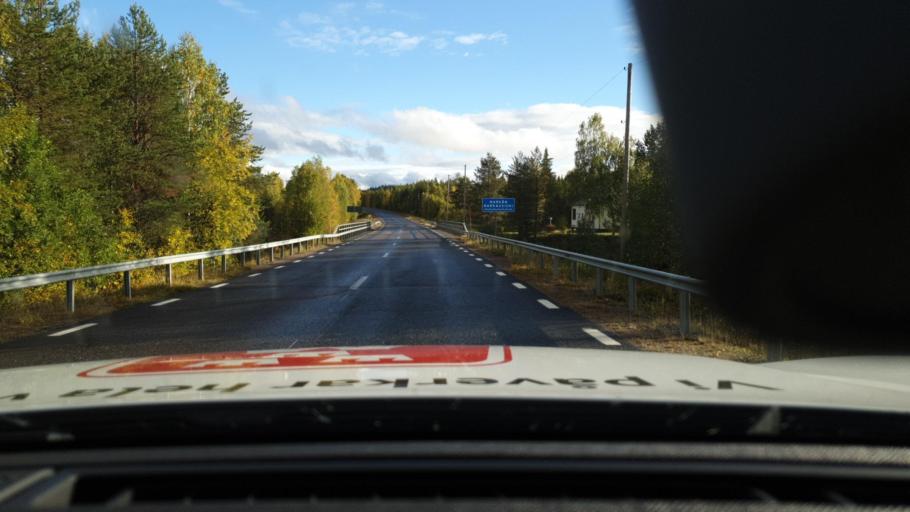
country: SE
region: Norrbotten
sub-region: Overkalix Kommun
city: OEverkalix
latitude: 66.9290
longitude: 22.7375
